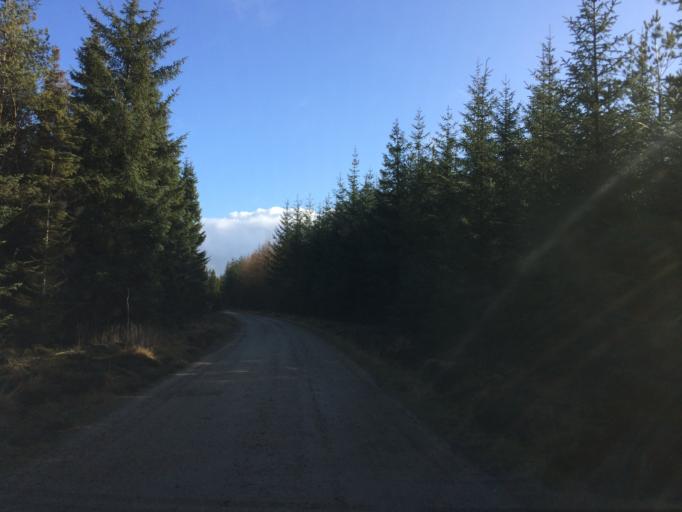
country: DK
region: Central Jutland
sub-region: Holstebro Kommune
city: Ulfborg
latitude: 56.2679
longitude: 8.3998
